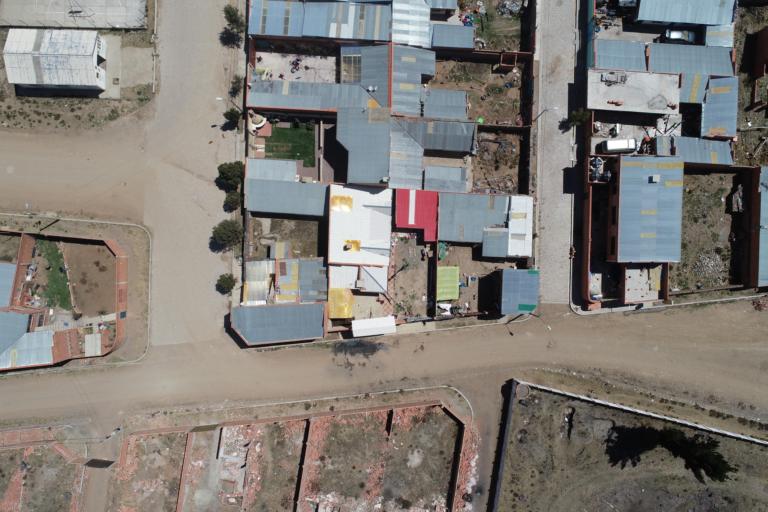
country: BO
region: La Paz
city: La Paz
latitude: -16.5677
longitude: -68.1931
